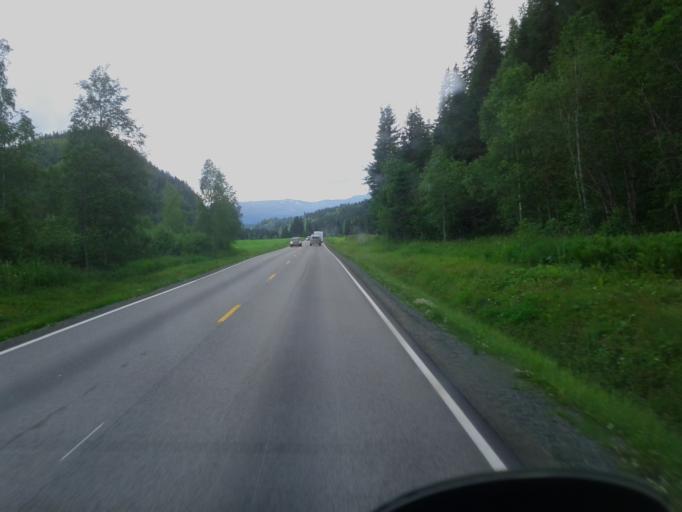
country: NO
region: Nord-Trondelag
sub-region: Grong
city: Grong
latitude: 64.5158
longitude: 12.3739
